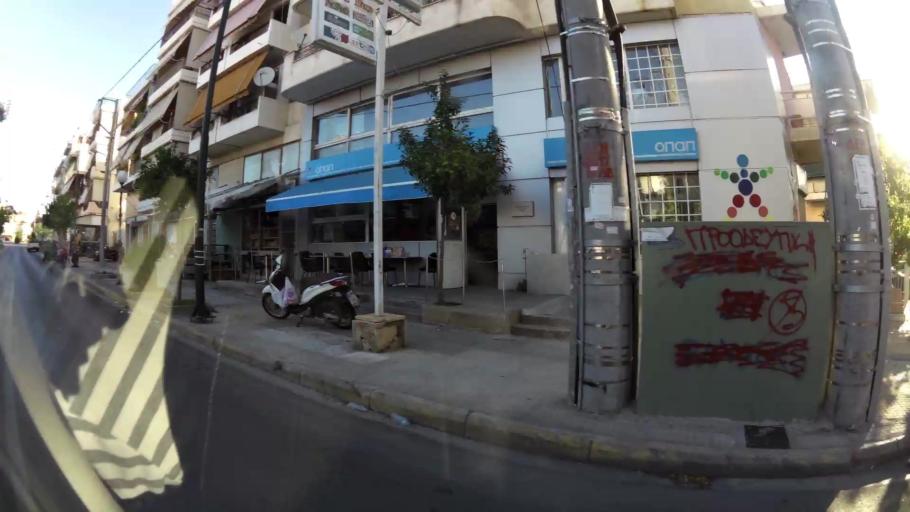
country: GR
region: Attica
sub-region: Nomarchia Athinas
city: Agia Varvara
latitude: 37.9771
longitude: 23.6609
